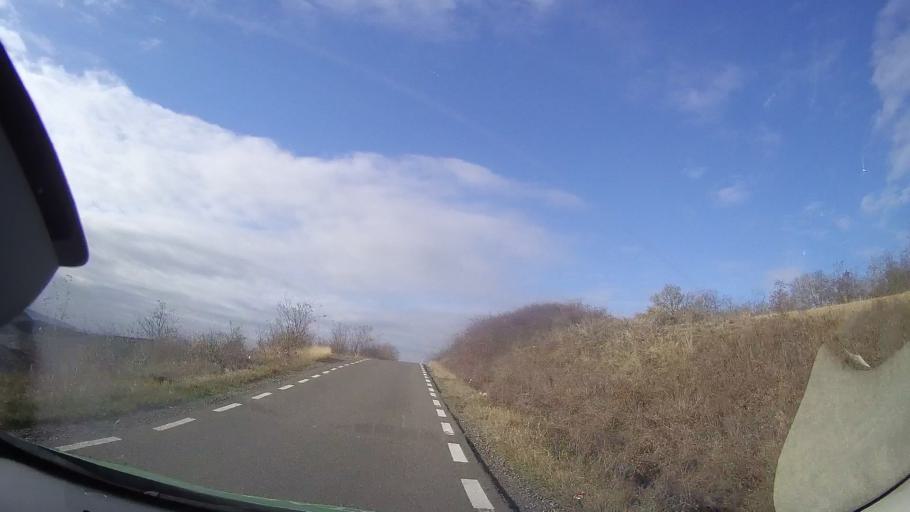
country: RO
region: Mures
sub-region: Comuna Papiu Ilarian
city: Papiu Ilarian
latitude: 46.5601
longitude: 24.1712
